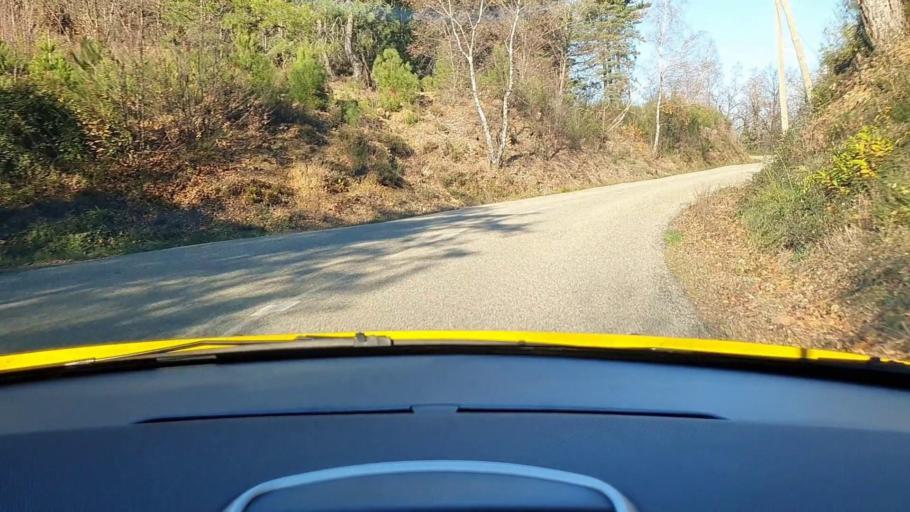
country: FR
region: Languedoc-Roussillon
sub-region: Departement du Gard
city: Branoux-les-Taillades
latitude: 44.2832
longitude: 3.9450
